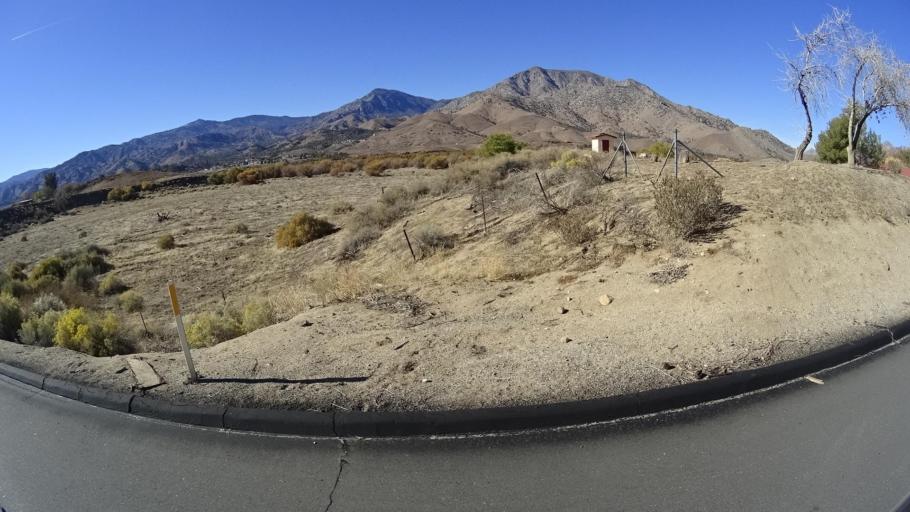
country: US
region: California
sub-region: Kern County
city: Wofford Heights
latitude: 35.7084
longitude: -118.4222
